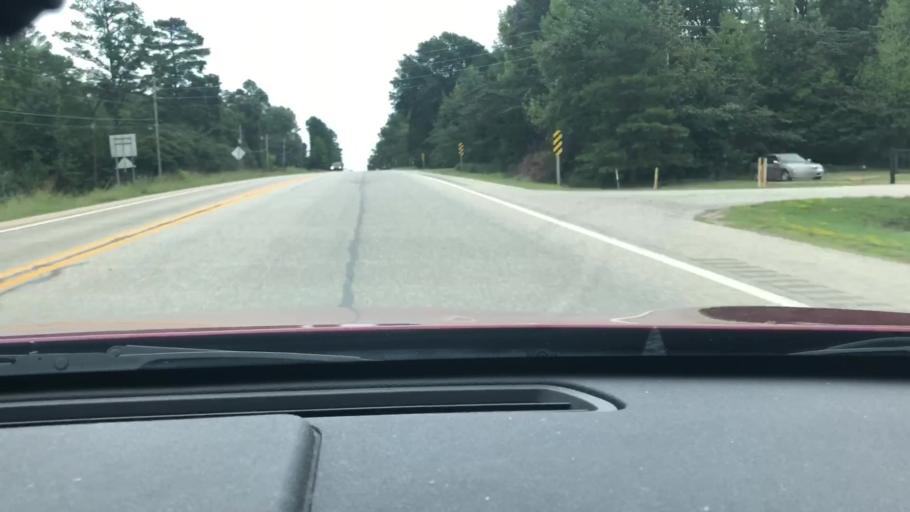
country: US
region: Arkansas
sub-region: Miller County
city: Texarkana
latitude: 33.4294
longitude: -93.9417
